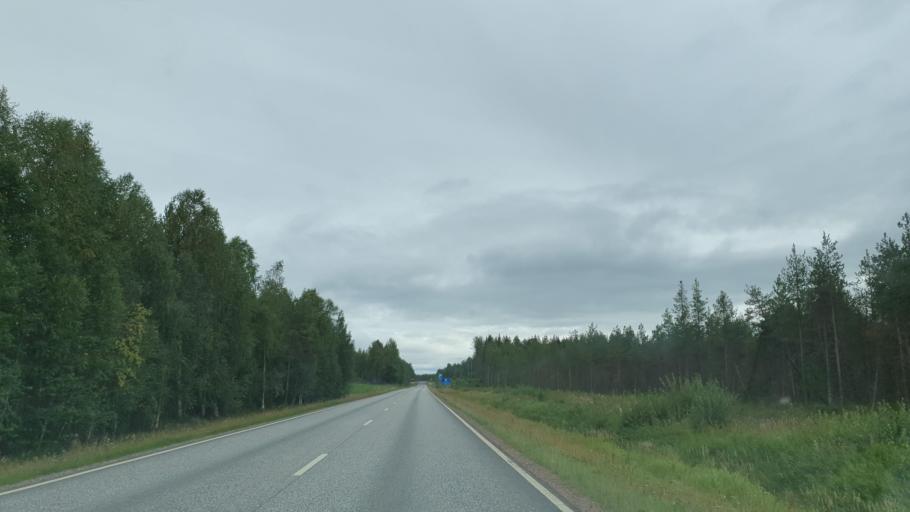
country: FI
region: Lapland
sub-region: Rovaniemi
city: Rovaniemi
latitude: 66.7970
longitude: 25.4148
